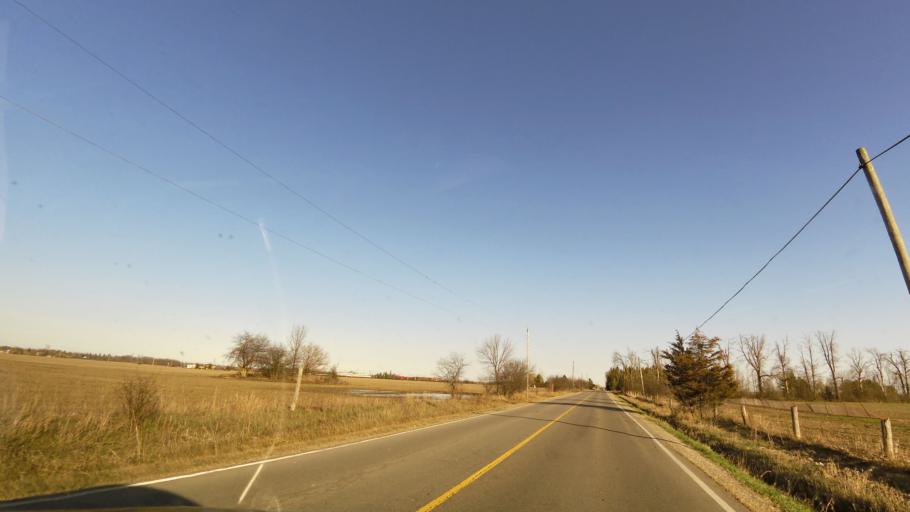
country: CA
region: Ontario
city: Brampton
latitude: 43.8300
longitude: -79.6941
